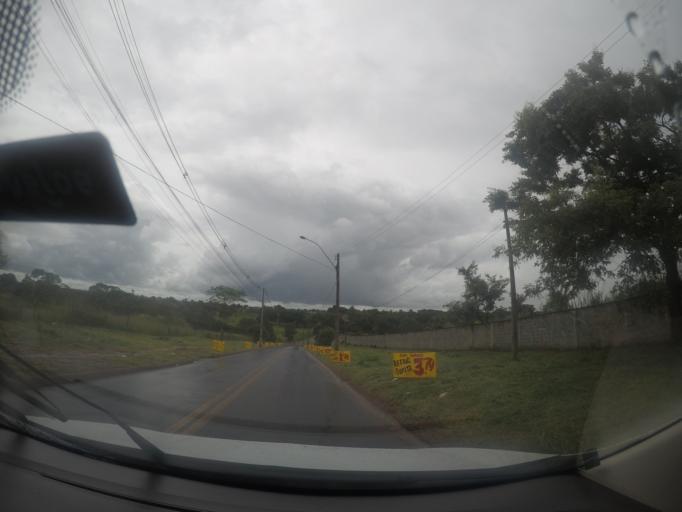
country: BR
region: Goias
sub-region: Trindade
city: Trindade
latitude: -16.6411
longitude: -49.4305
